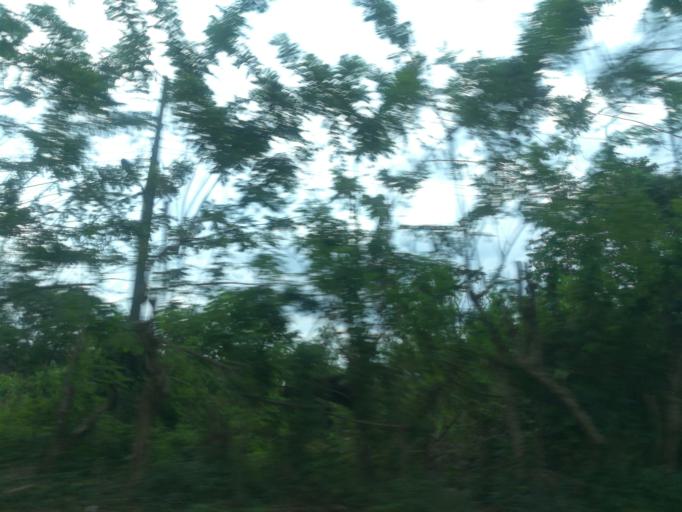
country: NG
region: Oyo
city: Ibadan
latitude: 7.4320
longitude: 3.8915
